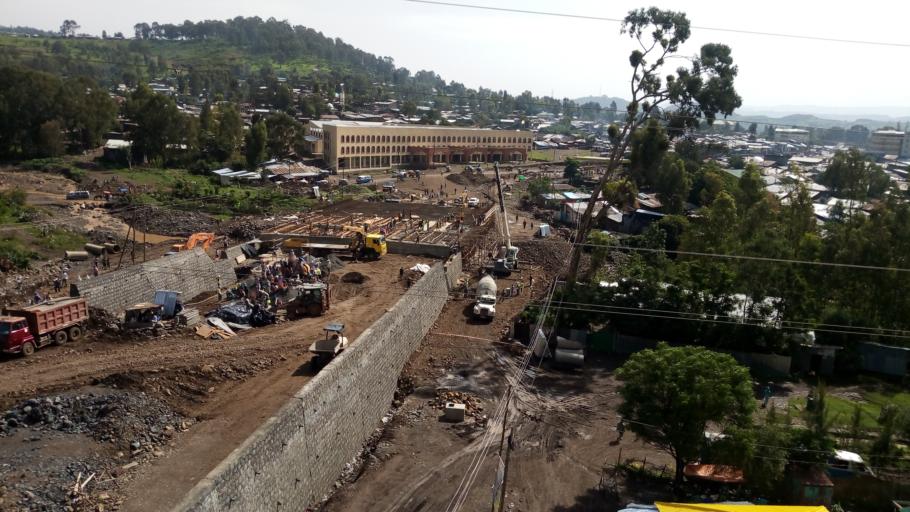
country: ET
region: Amhara
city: Gondar
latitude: 12.5512
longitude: 37.4250
